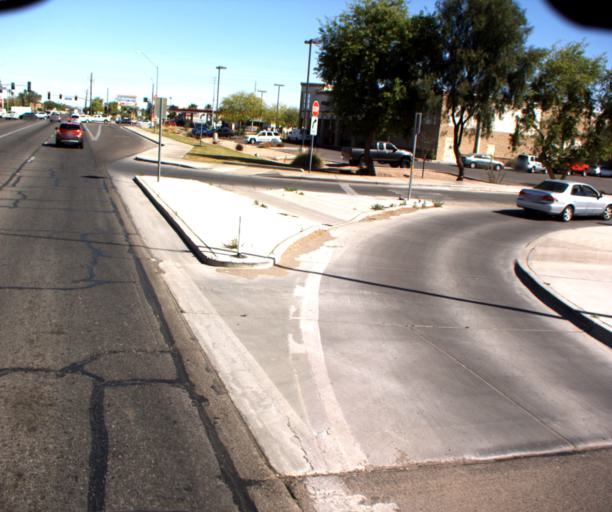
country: US
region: Arizona
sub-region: Yuma County
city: Yuma
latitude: 32.6825
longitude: -114.6503
